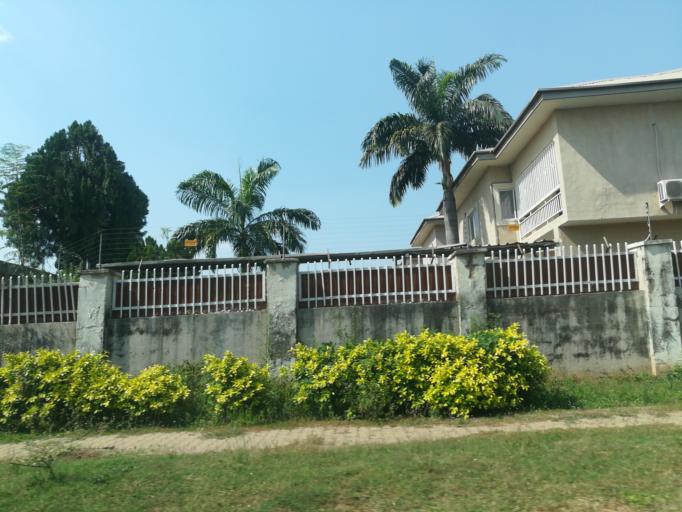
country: NG
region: Abuja Federal Capital Territory
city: Abuja
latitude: 9.0621
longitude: 7.4277
